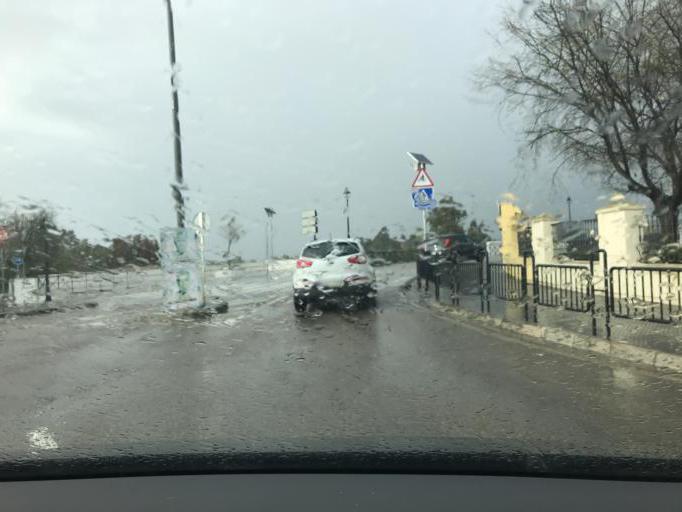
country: ES
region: Andalusia
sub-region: Provincia de Sevilla
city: Ecija
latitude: 37.5433
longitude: -5.0730
